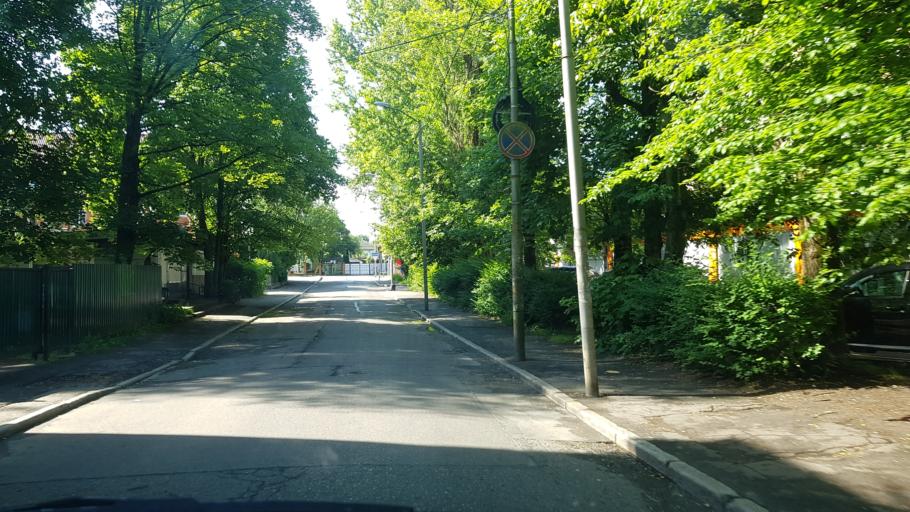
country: RU
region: Kaliningrad
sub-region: Gorod Kaliningrad
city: Kaliningrad
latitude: 54.7153
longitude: 20.4568
